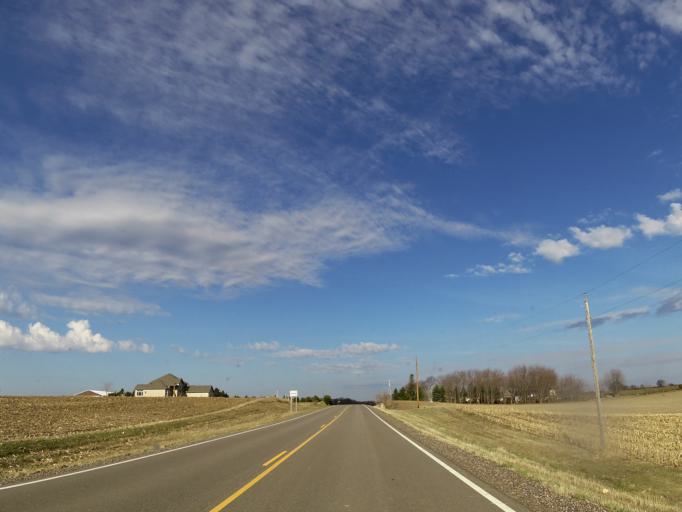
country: US
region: Minnesota
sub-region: Dakota County
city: Hastings
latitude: 44.8188
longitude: -92.8422
